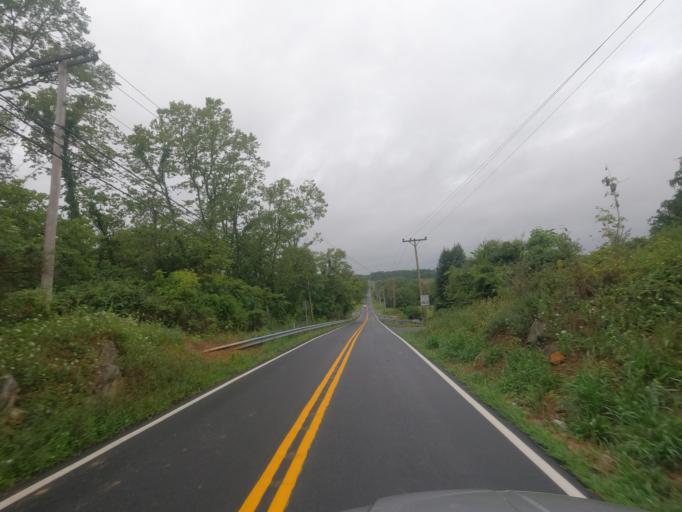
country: US
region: Maryland
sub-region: Washington County
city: Wilson-Conococheague
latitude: 39.6243
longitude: -77.9517
